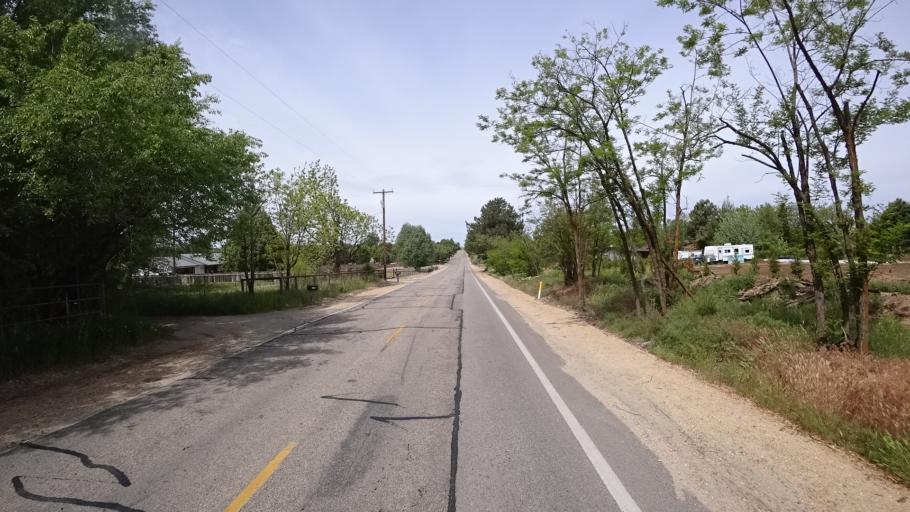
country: US
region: Idaho
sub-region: Ada County
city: Meridian
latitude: 43.5611
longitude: -116.3210
